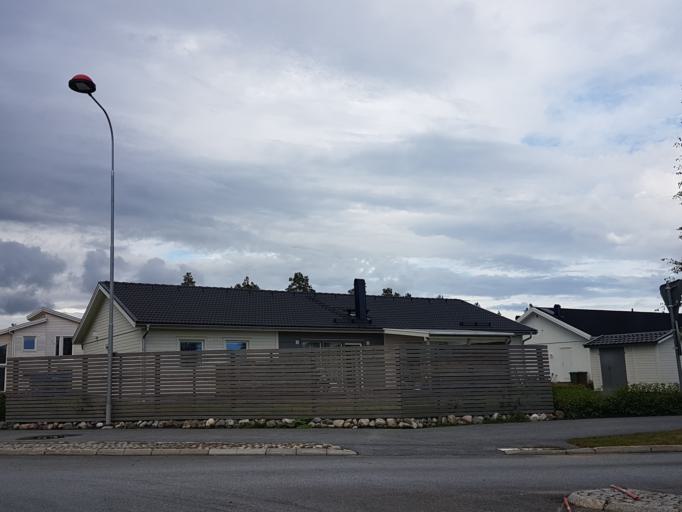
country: SE
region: Vaesterbotten
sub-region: Umea Kommun
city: Ersmark
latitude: 63.8028
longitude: 20.3696
